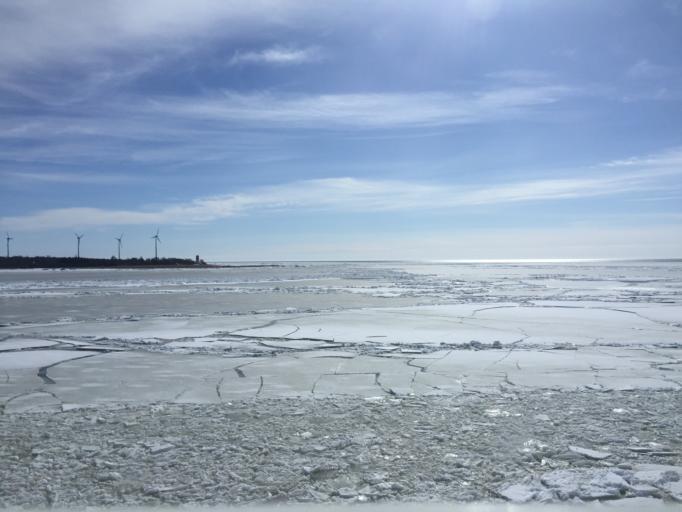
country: EE
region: Laeaene
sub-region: Lihula vald
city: Lihula
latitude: 58.5765
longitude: 23.4964
